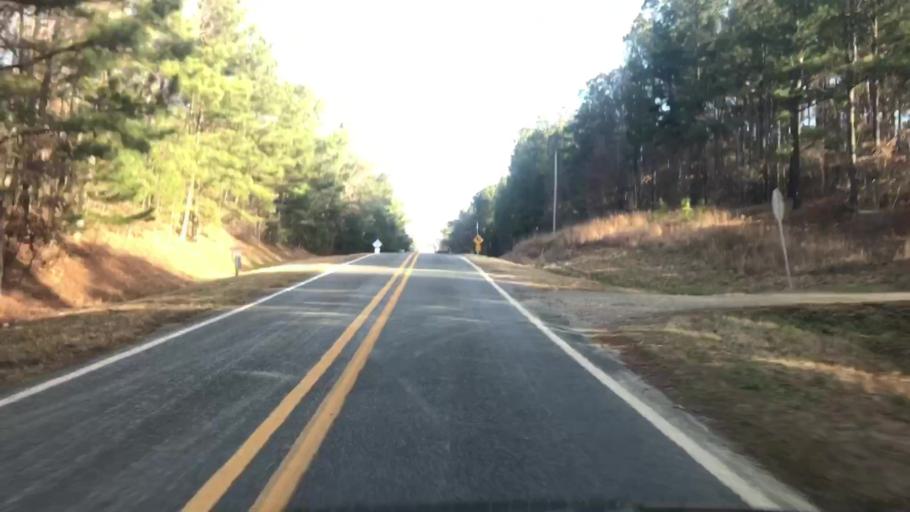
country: US
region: Arkansas
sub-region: Garland County
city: Rockwell
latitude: 34.4840
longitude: -93.2732
